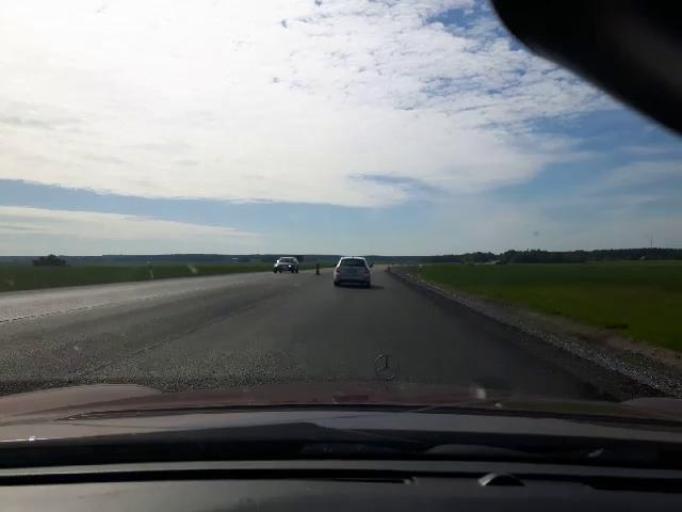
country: SE
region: Uppsala
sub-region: Enkopings Kommun
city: Irsta
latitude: 59.7510
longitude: 16.9435
